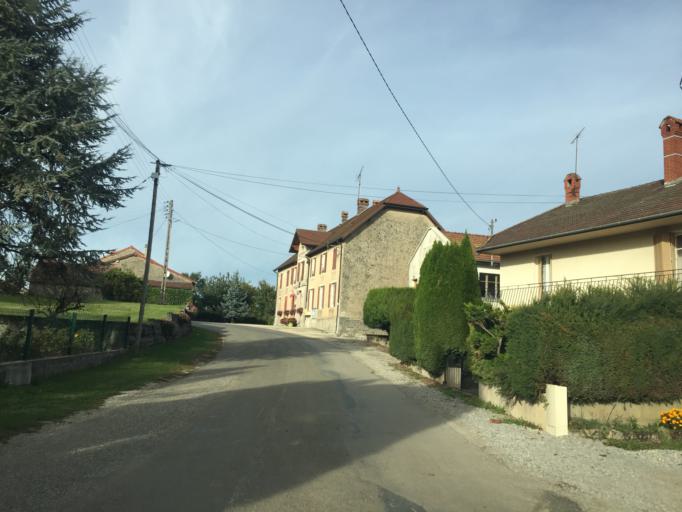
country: FR
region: Franche-Comte
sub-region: Departement du Jura
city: Orgelet
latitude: 46.5020
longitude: 5.5045
